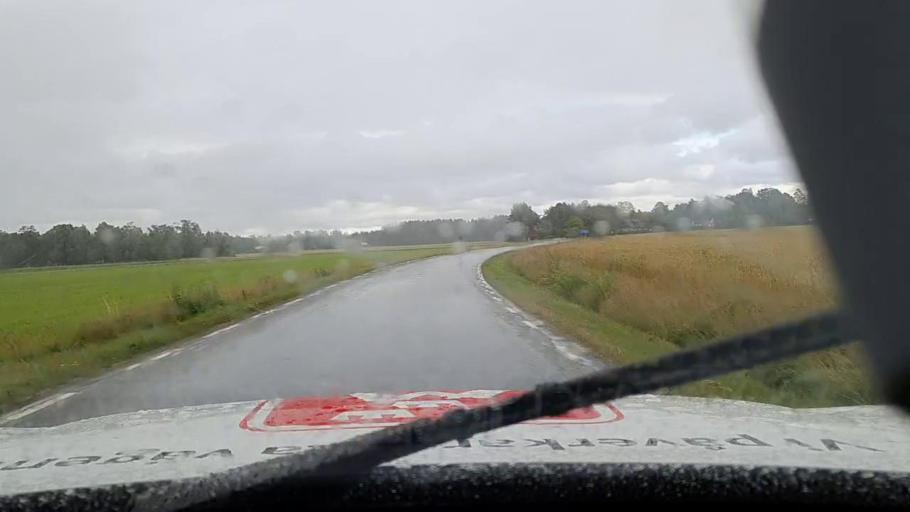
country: SE
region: Vaestra Goetaland
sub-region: Toreboda Kommun
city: Toereboda
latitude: 58.6584
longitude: 14.1236
